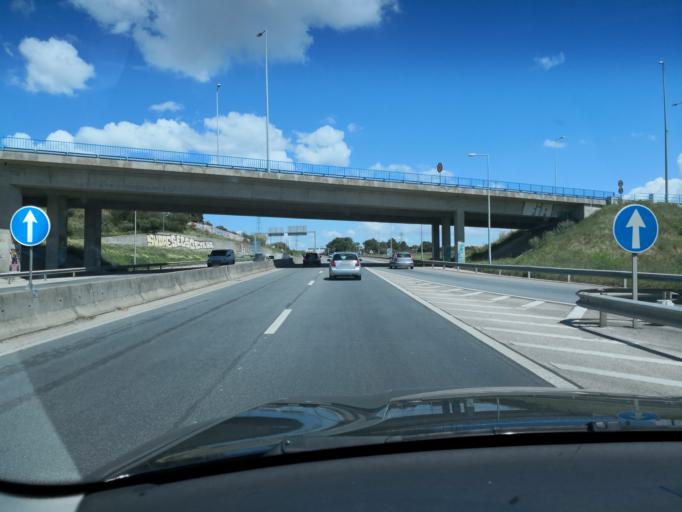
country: PT
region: Setubal
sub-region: Almada
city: Caparica
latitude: 38.6540
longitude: -9.2159
